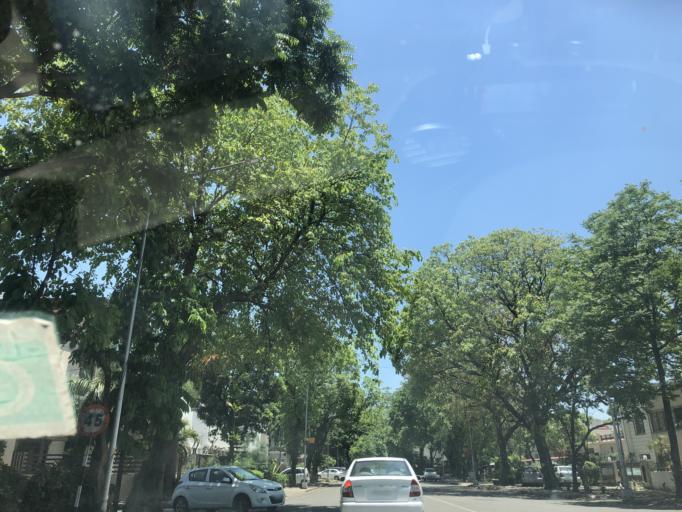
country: IN
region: Chandigarh
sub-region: Chandigarh
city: Chandigarh
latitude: 30.7565
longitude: 76.7872
